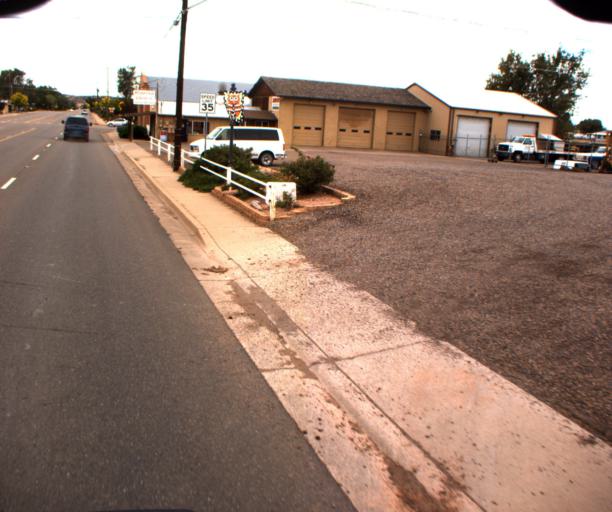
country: US
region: Arizona
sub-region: Navajo County
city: Taylor
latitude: 34.4660
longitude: -110.0913
